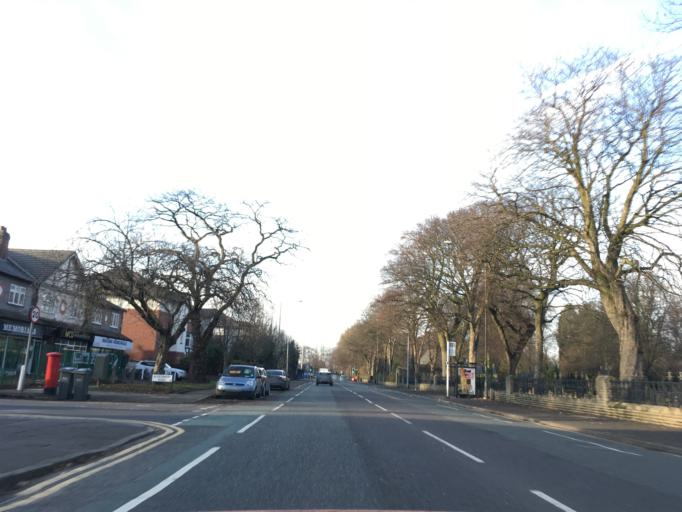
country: GB
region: England
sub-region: Manchester
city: Chorlton cum Hardy
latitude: 53.4269
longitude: -2.2597
